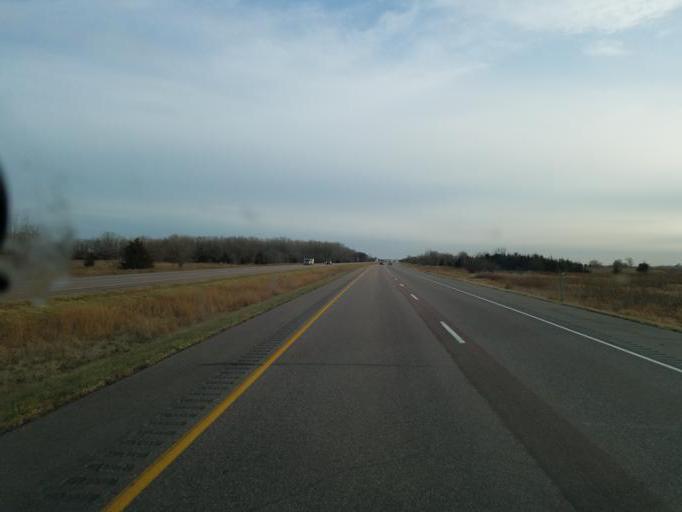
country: US
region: Nebraska
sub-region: Thurston County
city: Macy
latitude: 42.1398
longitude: -96.2120
